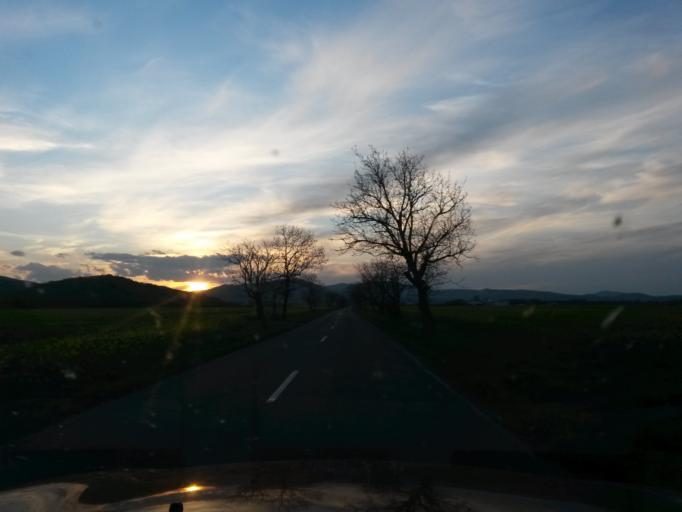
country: HU
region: Borsod-Abauj-Zemplen
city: Satoraljaujhely
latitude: 48.5141
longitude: 21.6052
